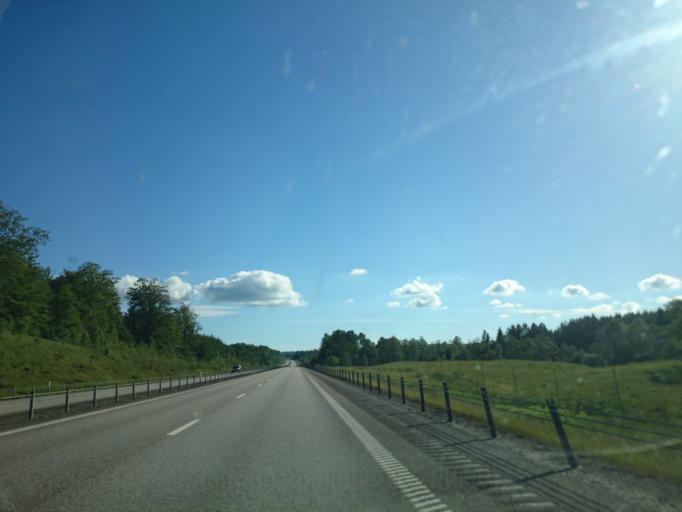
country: SE
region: Skane
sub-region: Orkelljunga Kommun
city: OErkelljunga
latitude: 56.3163
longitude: 13.4154
